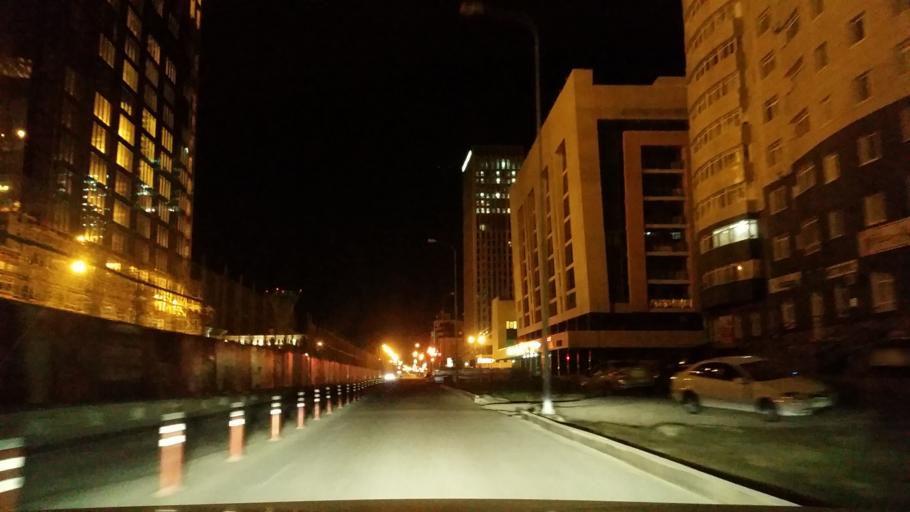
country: KZ
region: Astana Qalasy
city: Astana
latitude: 51.1210
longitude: 71.4296
